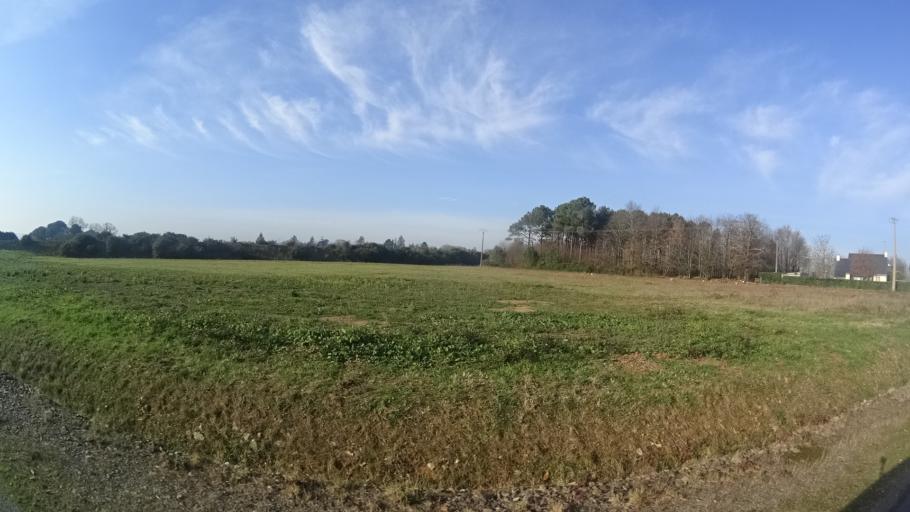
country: FR
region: Brittany
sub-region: Departement du Morbihan
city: Allaire
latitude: 47.6140
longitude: -2.1471
